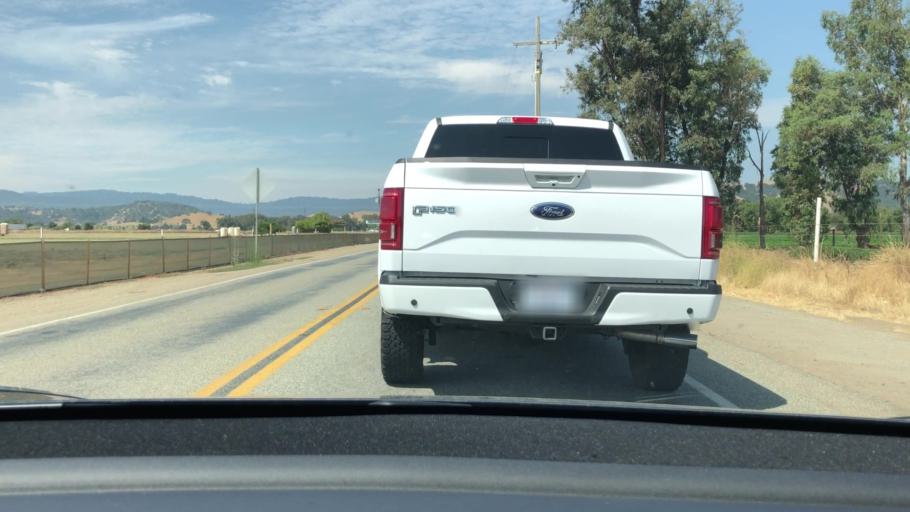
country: US
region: California
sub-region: Santa Clara County
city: San Martin
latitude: 37.0580
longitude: -121.5884
